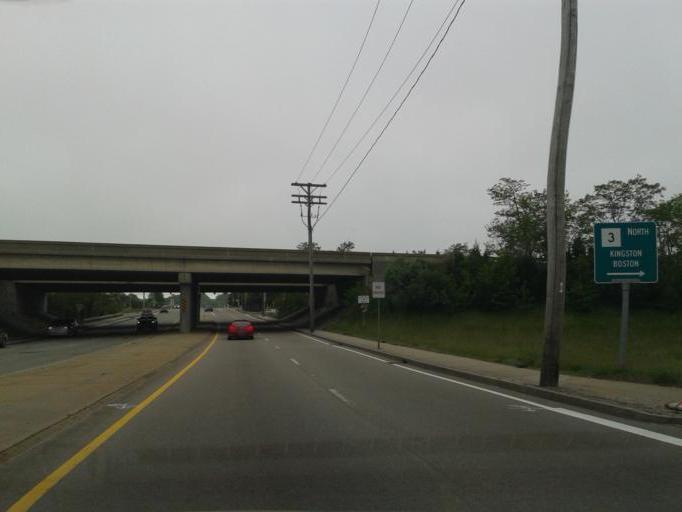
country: US
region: Massachusetts
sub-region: Plymouth County
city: Plymouth
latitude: 41.9550
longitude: -70.6815
